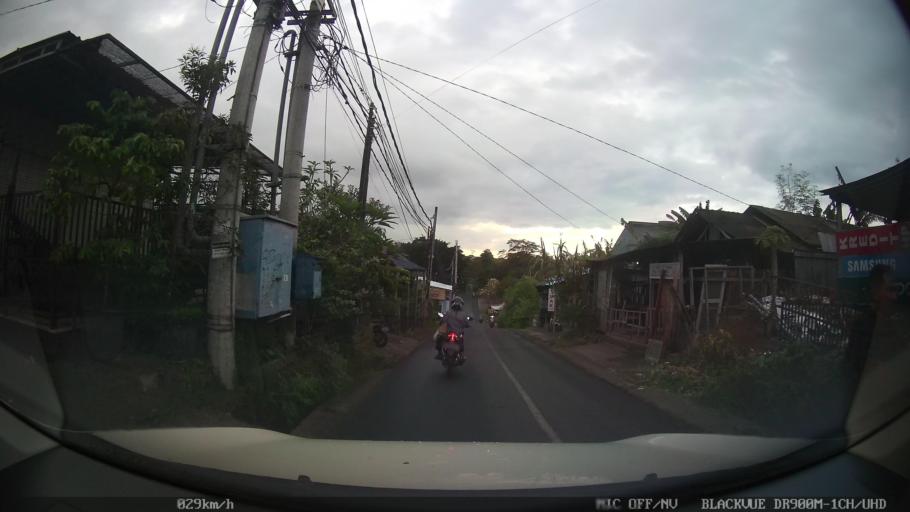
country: ID
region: Bali
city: Banjar Paangkelod
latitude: -8.6185
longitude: 115.2619
